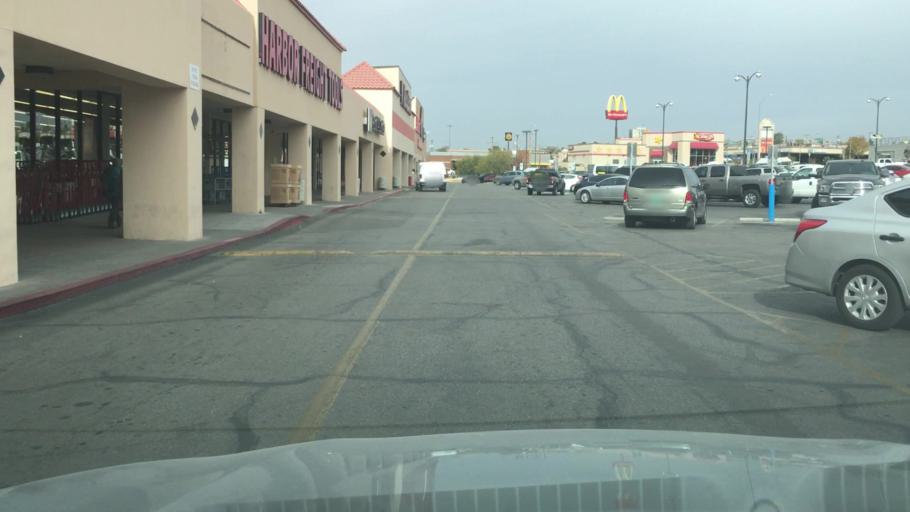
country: US
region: New Mexico
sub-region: Dona Ana County
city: Sunland Park
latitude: 31.8288
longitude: -106.5298
